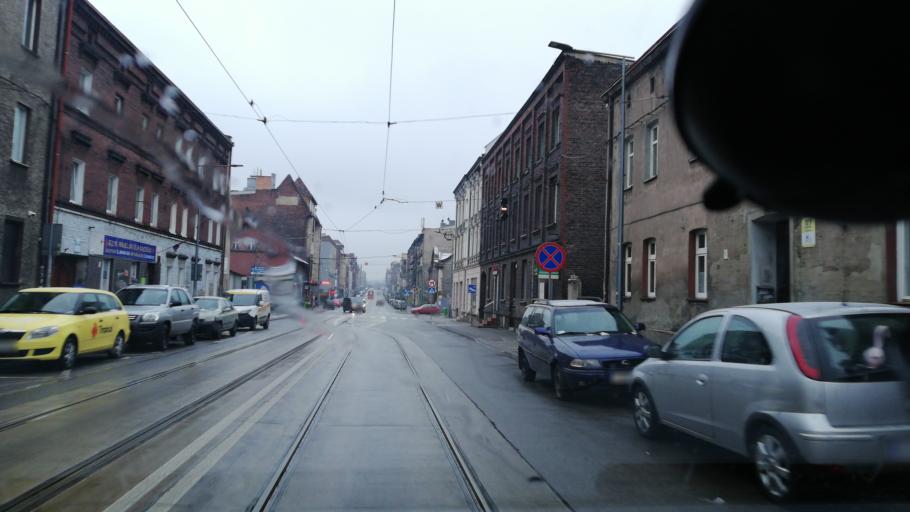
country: PL
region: Silesian Voivodeship
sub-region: Swietochlowice
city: Swietochlowice
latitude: 50.2909
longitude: 18.9448
